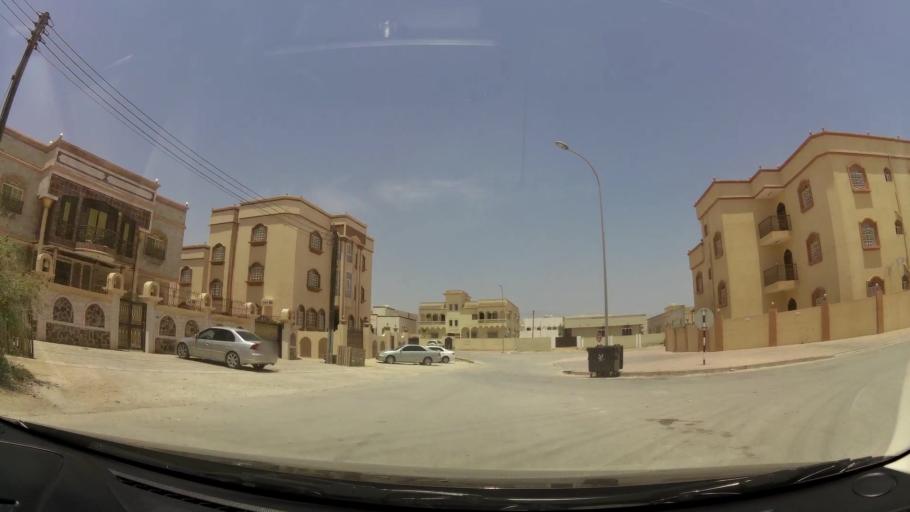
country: OM
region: Zufar
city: Salalah
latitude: 17.0707
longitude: 54.1573
